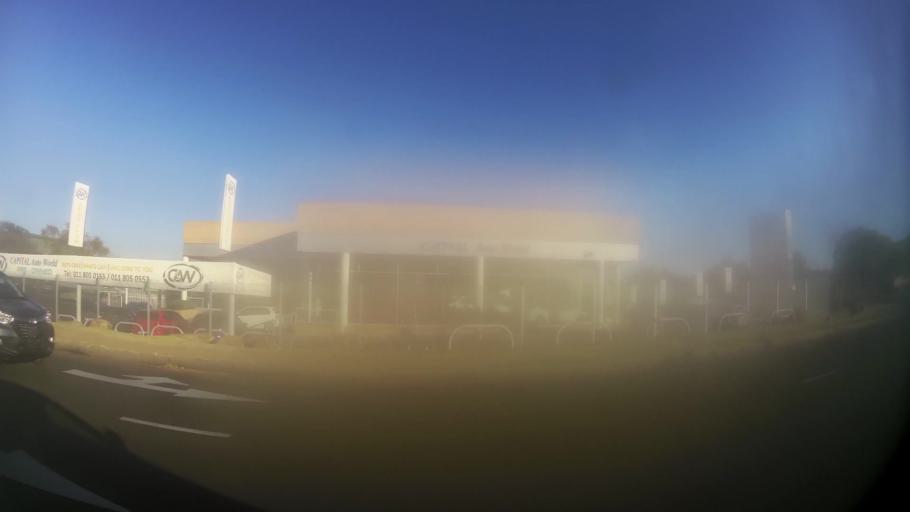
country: ZA
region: Gauteng
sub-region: City of Johannesburg Metropolitan Municipality
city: Midrand
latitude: -25.9896
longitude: 28.1305
